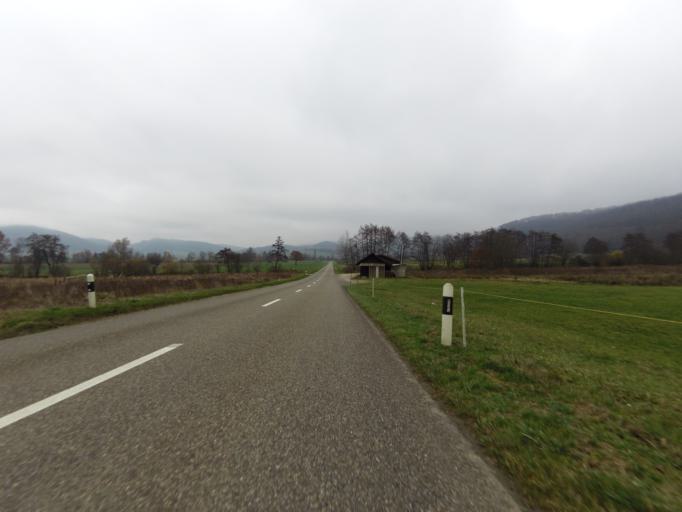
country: CH
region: Jura
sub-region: Porrentruy District
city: Alle
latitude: 47.4117
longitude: 7.1770
